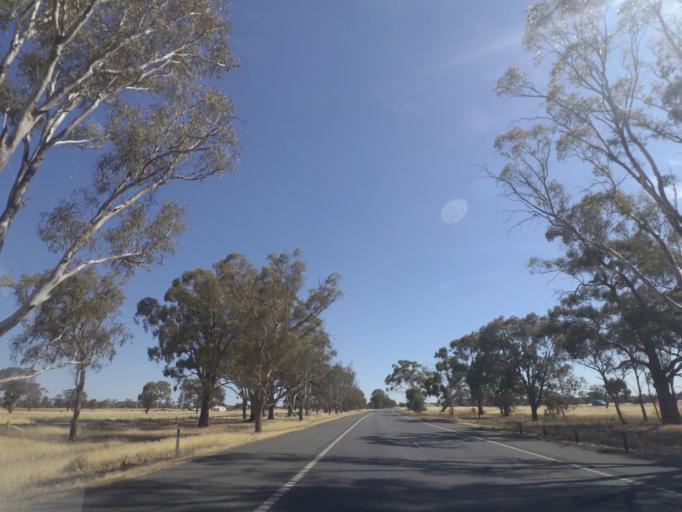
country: AU
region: Victoria
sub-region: Greater Shepparton
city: Shepparton
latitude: -36.6049
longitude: 145.3234
